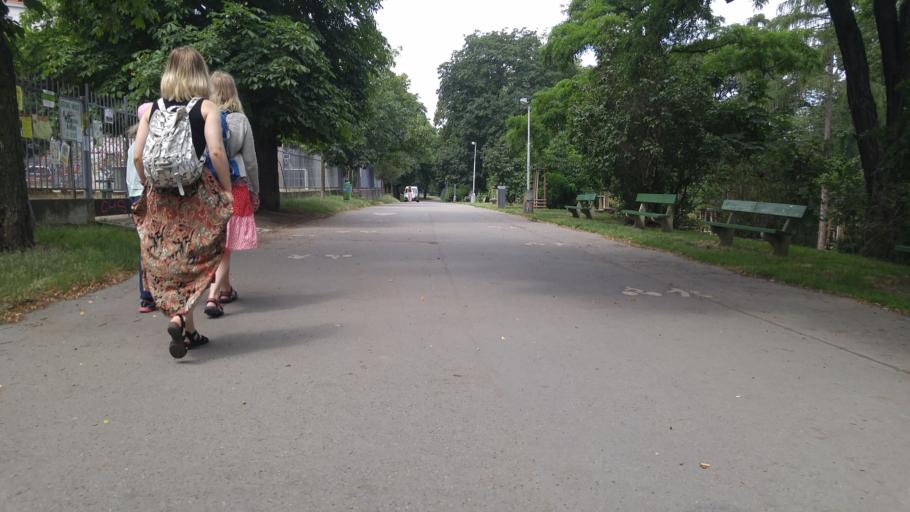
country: CZ
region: Praha
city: Prague
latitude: 50.1031
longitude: 14.4214
